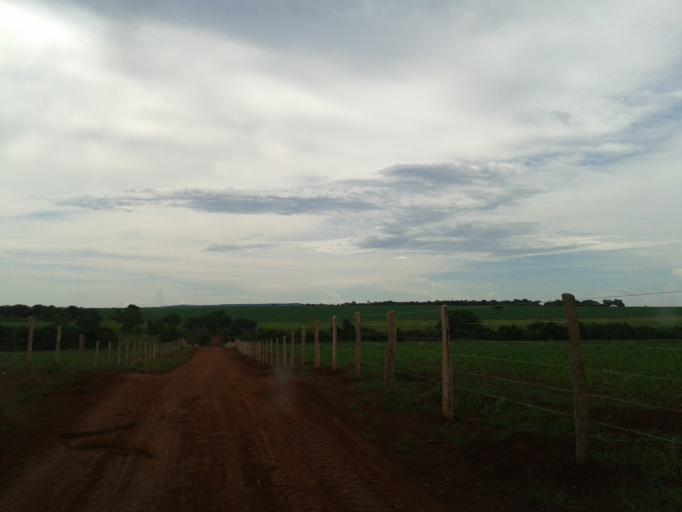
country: BR
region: Minas Gerais
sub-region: Centralina
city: Centralina
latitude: -18.6731
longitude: -49.3488
